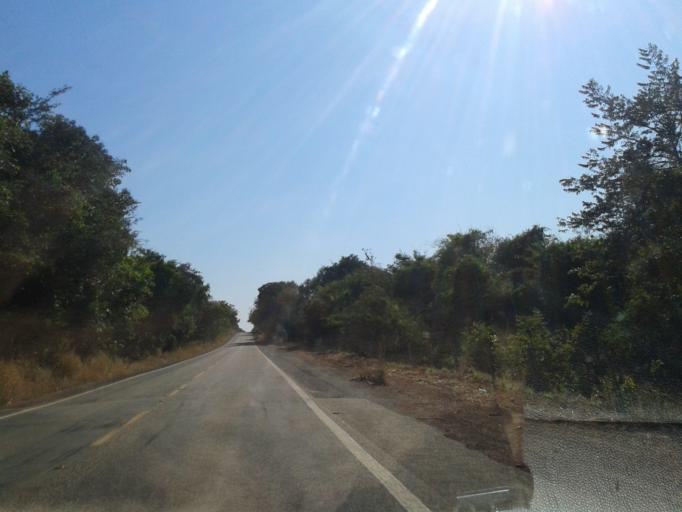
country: BR
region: Goias
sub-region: Mozarlandia
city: Mozarlandia
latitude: -14.6944
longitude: -50.5443
